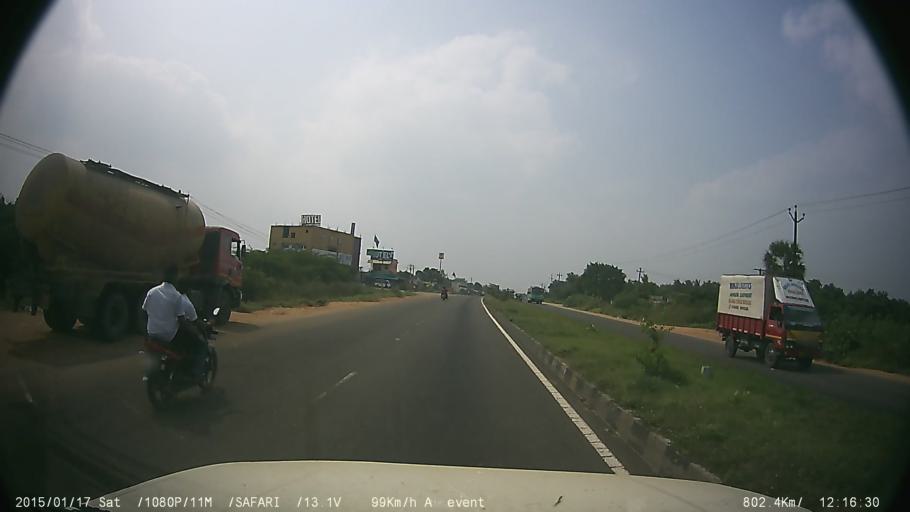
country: IN
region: Tamil Nadu
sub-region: Kancheepuram
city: Sriperumbudur
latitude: 12.9154
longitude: 79.8584
